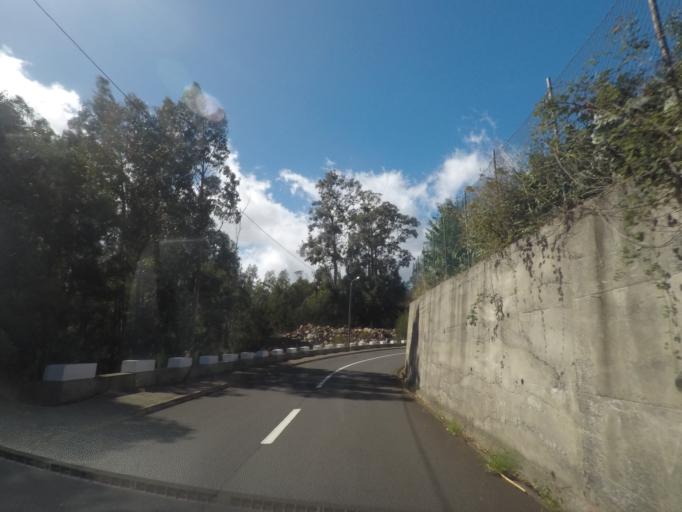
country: PT
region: Madeira
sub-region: Ribeira Brava
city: Campanario
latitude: 32.6823
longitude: -17.0415
